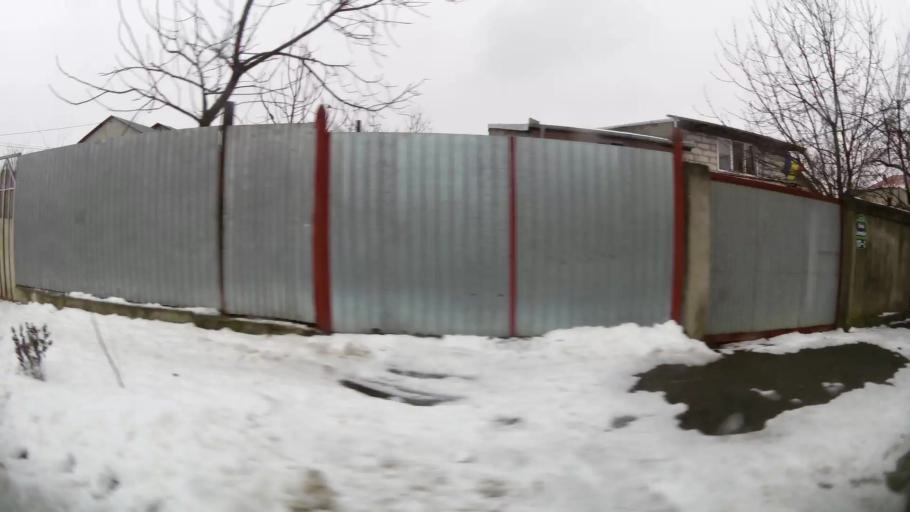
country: RO
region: Ilfov
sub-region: Comuna Mogosoaia
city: Mogosoaia
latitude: 44.5122
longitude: 26.0277
